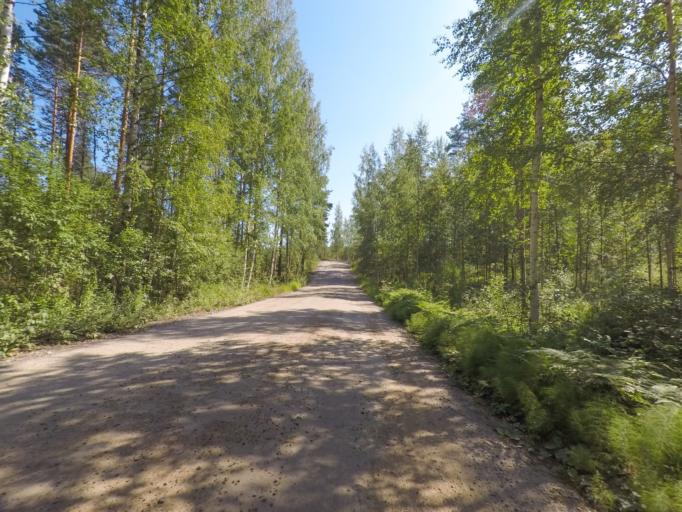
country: FI
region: Southern Savonia
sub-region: Mikkeli
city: Puumala
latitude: 61.4128
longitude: 28.0479
